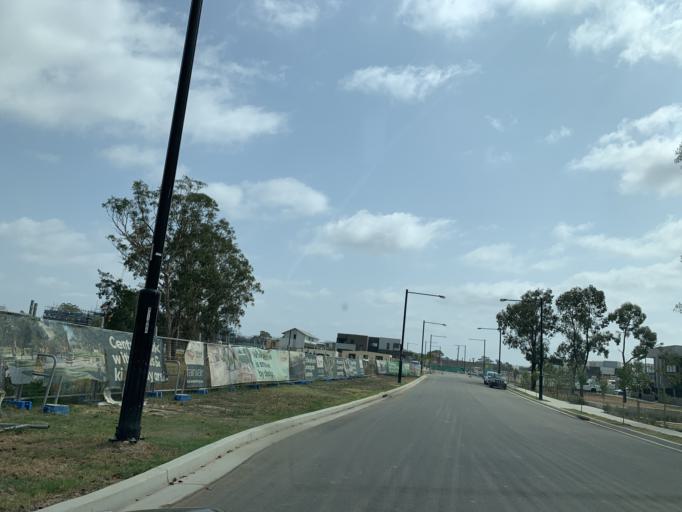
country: AU
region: New South Wales
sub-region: Blacktown
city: Blacktown
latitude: -33.7565
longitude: 150.9016
